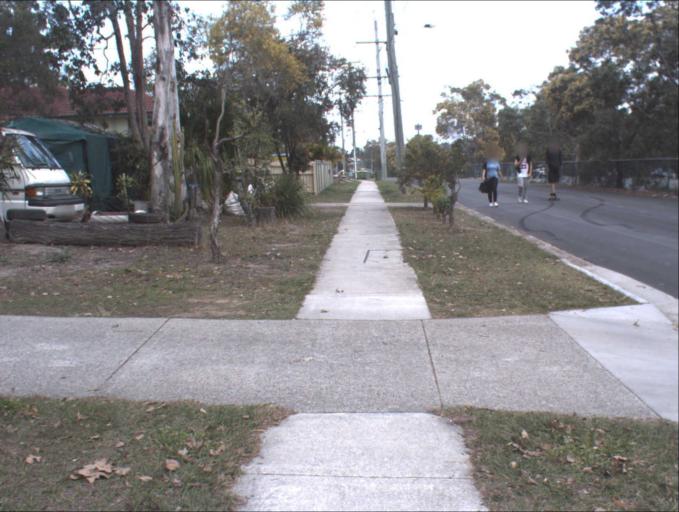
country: AU
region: Queensland
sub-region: Logan
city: Waterford West
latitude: -27.6717
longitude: 153.1226
